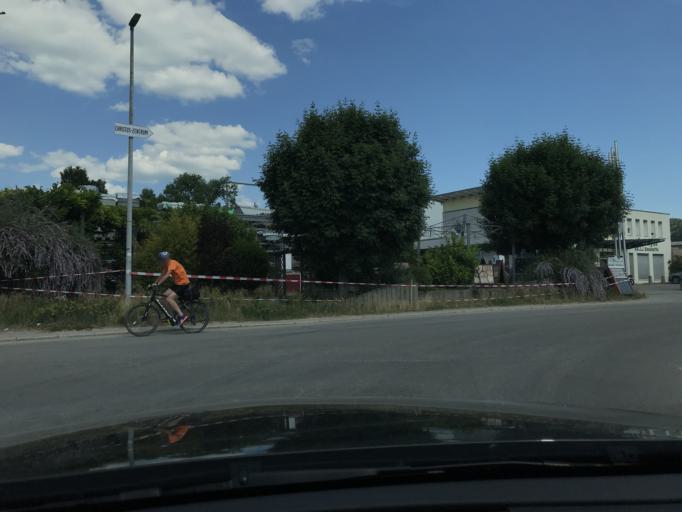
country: DE
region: Baden-Wuerttemberg
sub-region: Regierungsbezirk Stuttgart
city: Weinstadt-Endersbach
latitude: 48.8119
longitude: 9.3884
